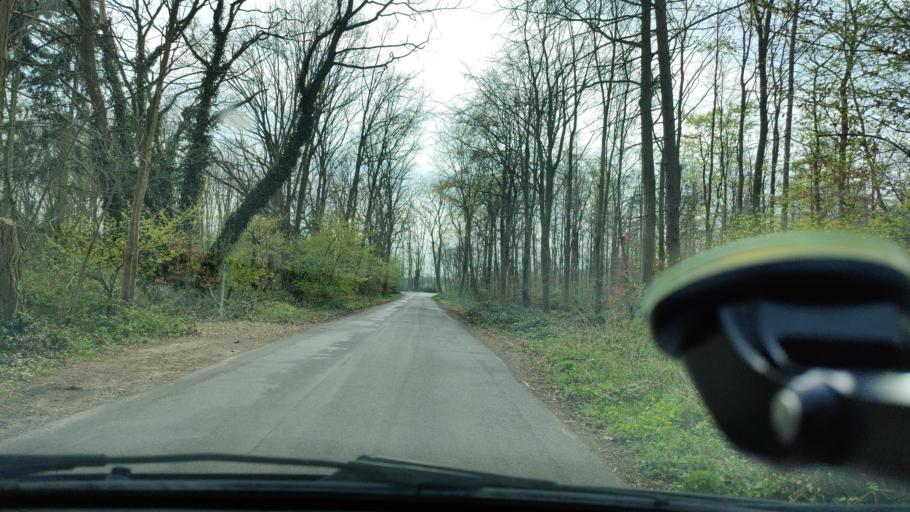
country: DE
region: North Rhine-Westphalia
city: Rheinberg
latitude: 51.5275
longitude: 6.6419
